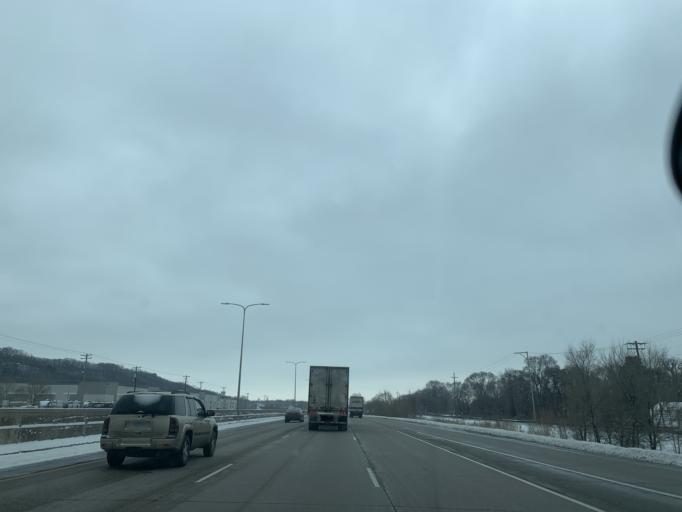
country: US
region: Minnesota
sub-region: Washington County
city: Newport
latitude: 44.8668
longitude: -92.9990
